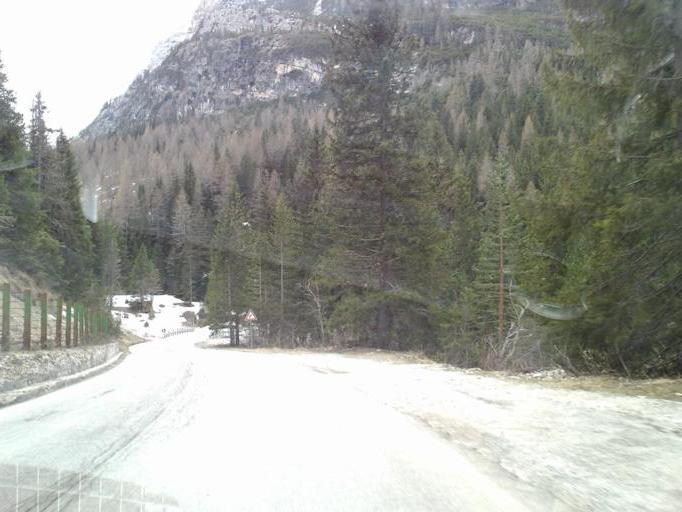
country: IT
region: Veneto
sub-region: Provincia di Belluno
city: Cortina d'Ampezzo
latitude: 46.5991
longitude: 12.2431
